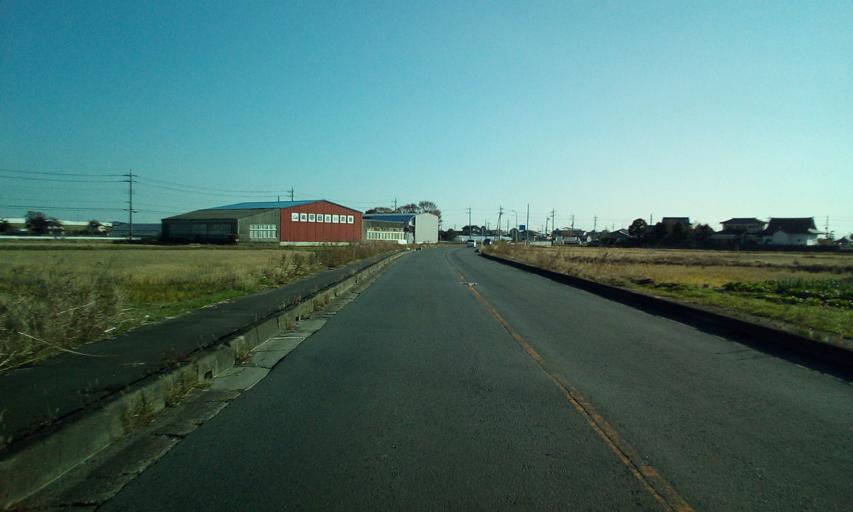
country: JP
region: Saitama
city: Yoshikawa
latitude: 35.8931
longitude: 139.8794
